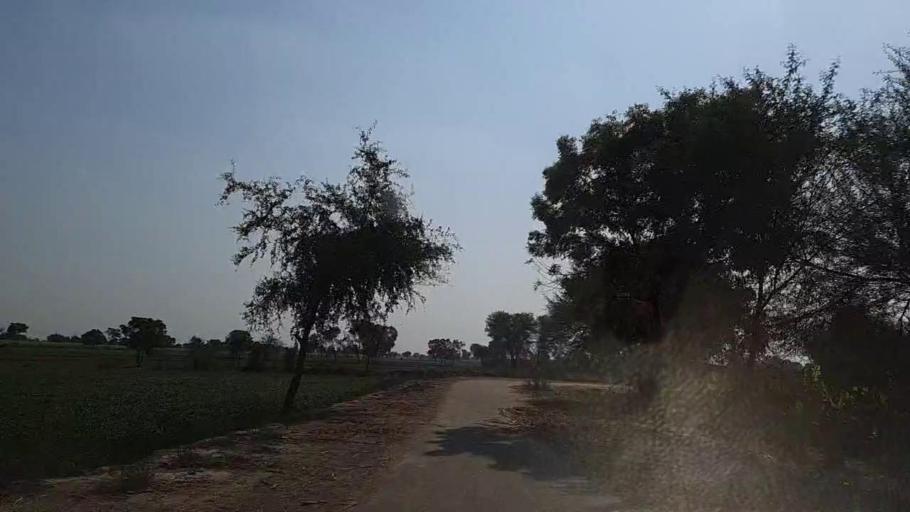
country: PK
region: Sindh
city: Daur
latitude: 26.4890
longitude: 68.2518
